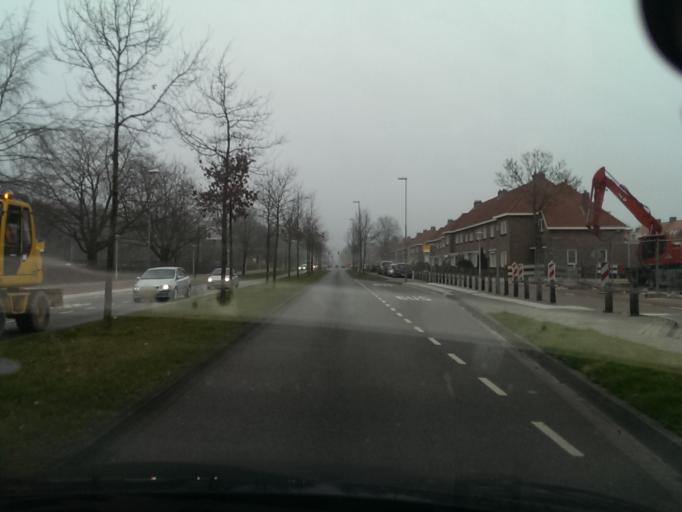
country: NL
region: North Brabant
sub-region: Gemeente Eindhoven
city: Eindhoven
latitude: 51.4598
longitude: 5.4564
